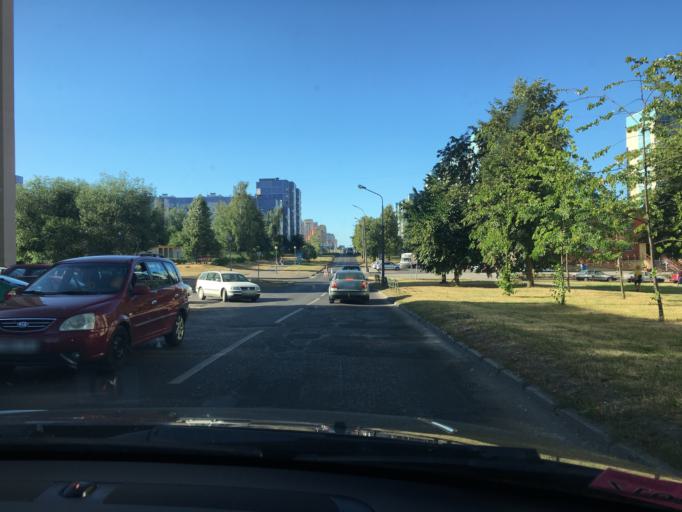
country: BY
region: Grodnenskaya
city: Hrodna
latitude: 53.7028
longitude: 23.8496
